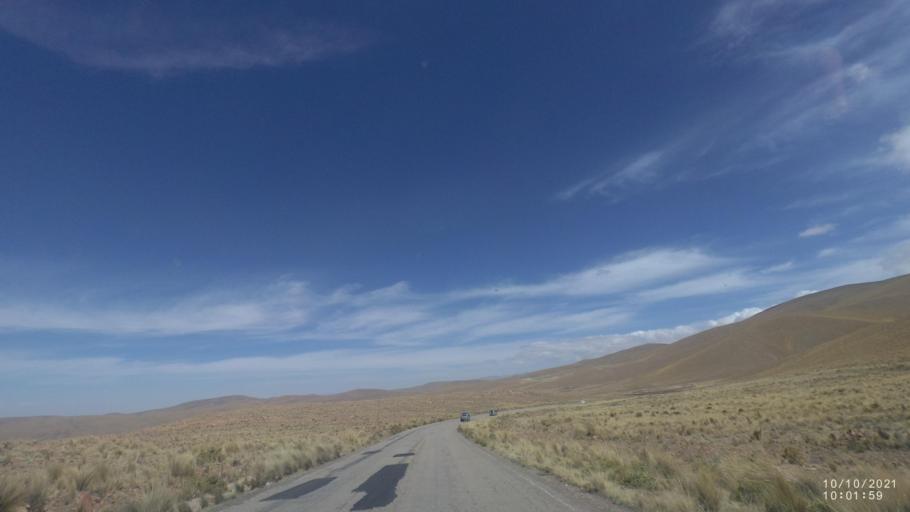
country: BO
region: La Paz
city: Eucaliptus
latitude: -17.3638
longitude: -67.4282
